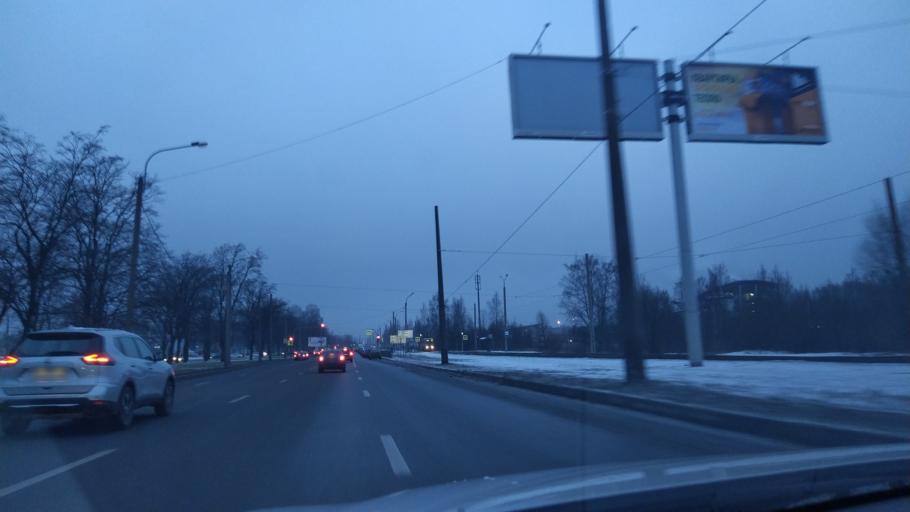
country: RU
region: St.-Petersburg
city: Grazhdanka
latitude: 60.0208
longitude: 30.4325
